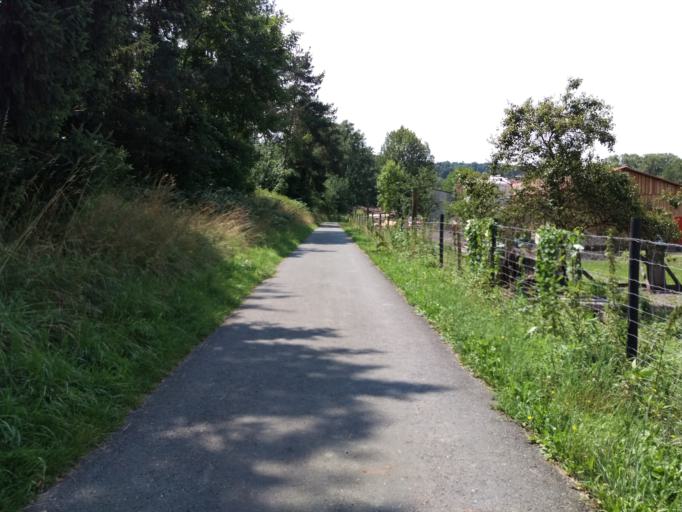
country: AT
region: Styria
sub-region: Politischer Bezirk Graz-Umgebung
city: Hart bei Graz
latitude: 47.0480
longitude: 15.5333
